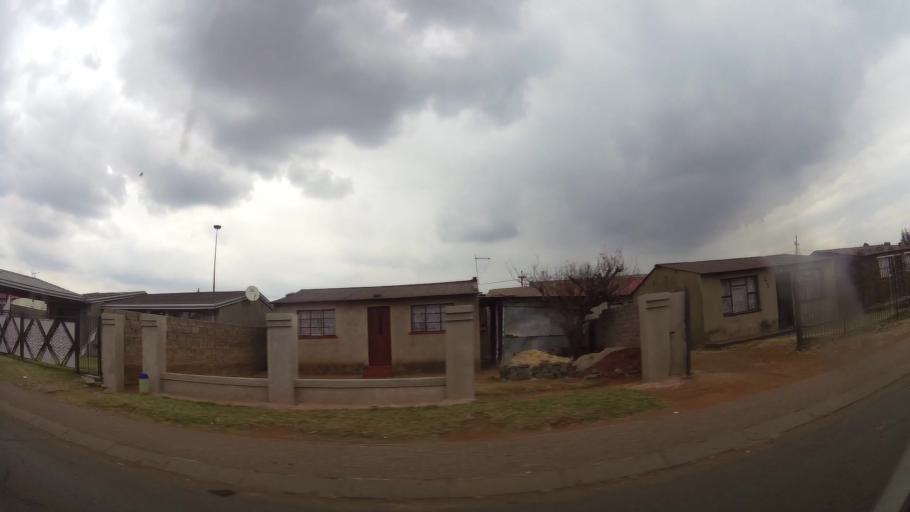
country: ZA
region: Gauteng
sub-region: Ekurhuleni Metropolitan Municipality
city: Germiston
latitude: -26.3319
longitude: 28.1498
